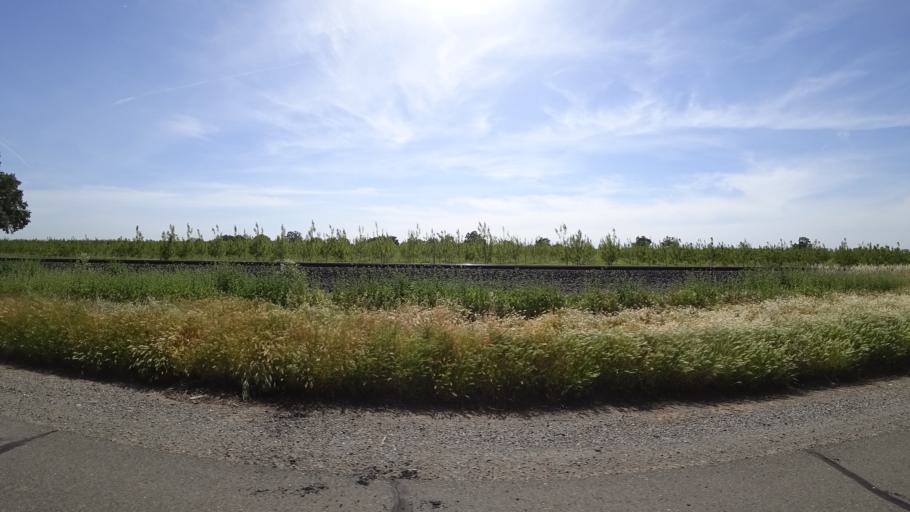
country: US
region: California
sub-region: Tehama County
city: Los Molinos
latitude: 40.0005
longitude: -122.0896
